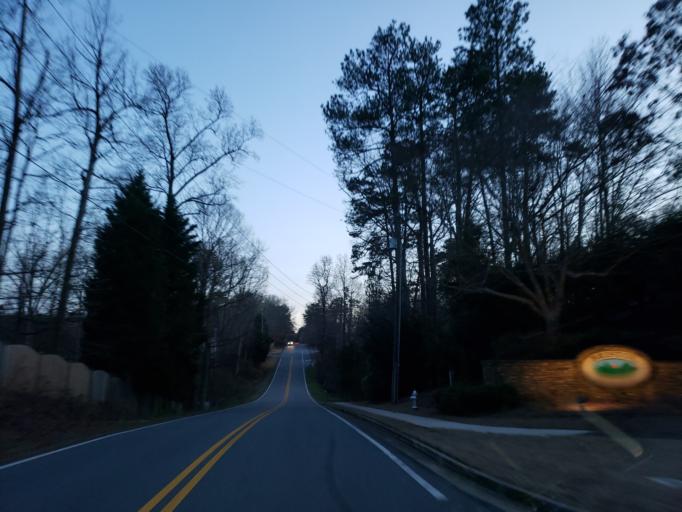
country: US
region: Georgia
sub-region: Cobb County
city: Kennesaw
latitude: 34.0010
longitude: -84.6345
